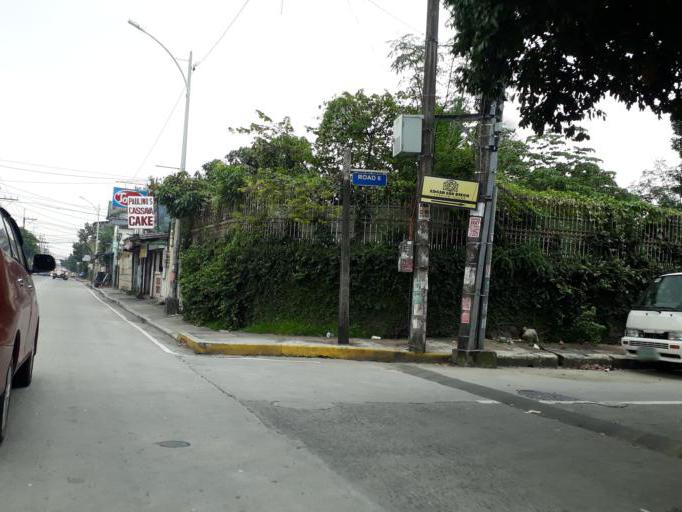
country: PH
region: Calabarzon
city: Bagong Pagasa
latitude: 14.6606
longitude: 121.0392
